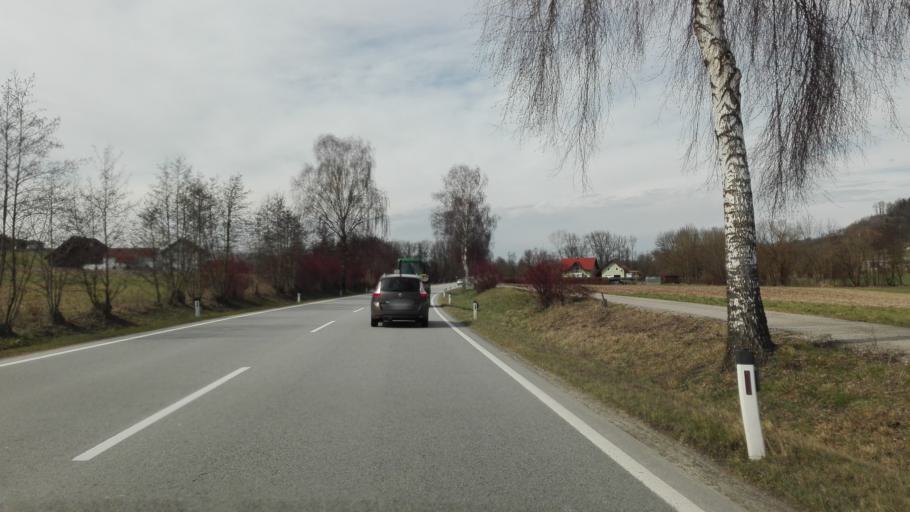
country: AT
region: Upper Austria
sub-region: Politischer Bezirk Scharding
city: Sankt Marienkirchen bei Schaerding
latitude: 48.4038
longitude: 13.4827
